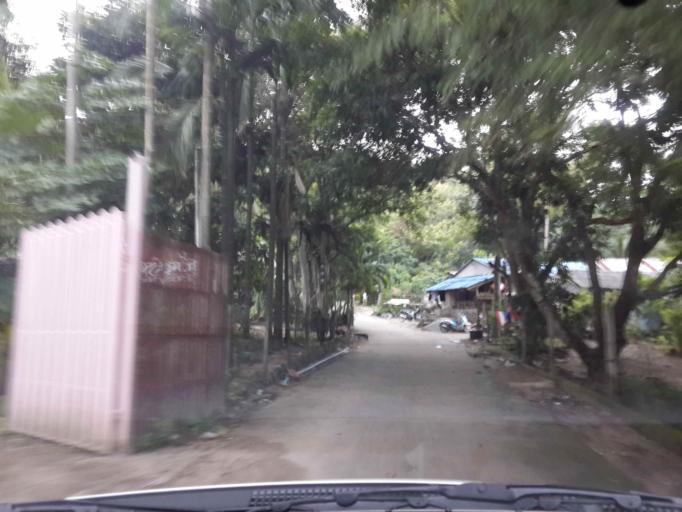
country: TH
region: Ratchaburi
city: Suan Phueng
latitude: 13.5925
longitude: 99.2050
